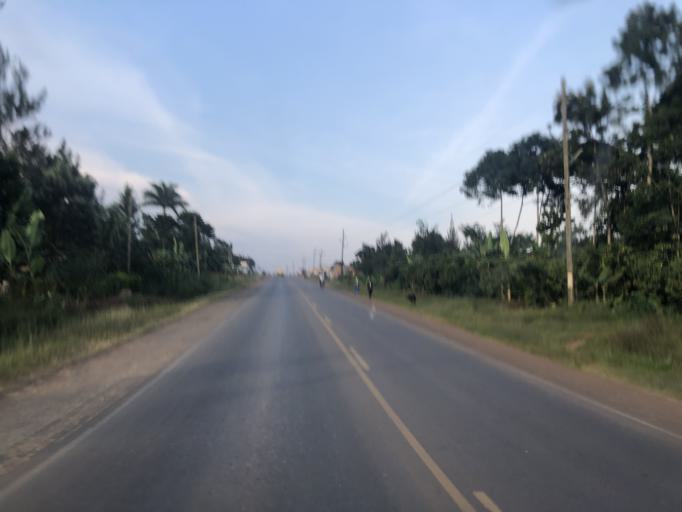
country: UG
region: Central Region
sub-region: Mpigi District
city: Mpigi
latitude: 0.2052
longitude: 32.3118
